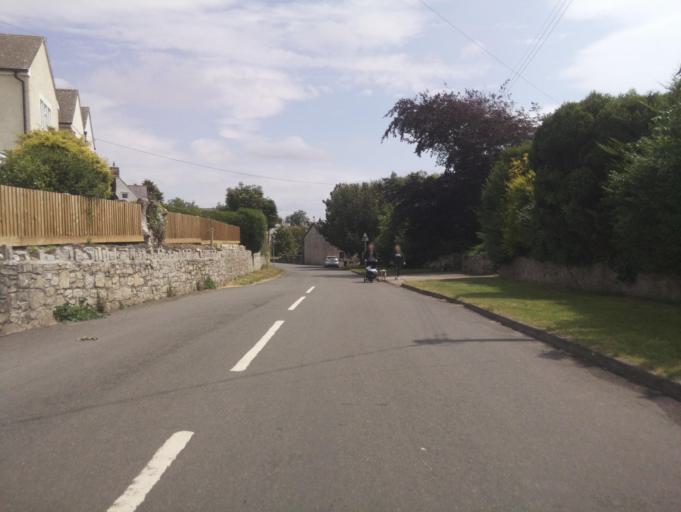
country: GB
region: Wales
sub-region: Vale of Glamorgan
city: Llantwit Major
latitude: 51.4090
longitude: -3.4903
